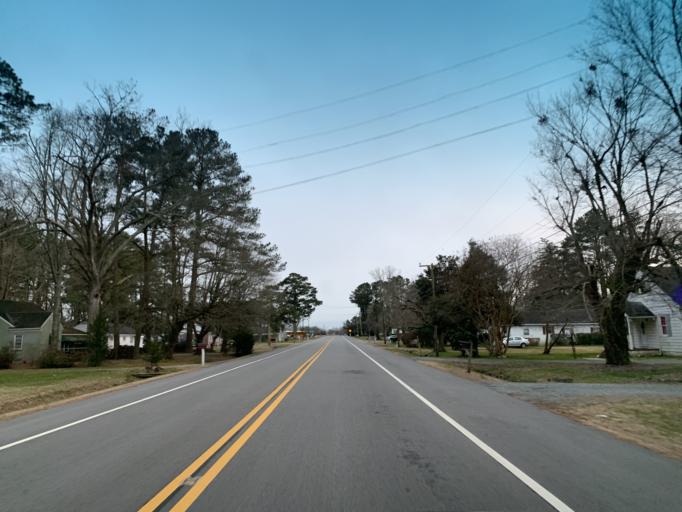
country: US
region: Maryland
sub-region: Worcester County
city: Pocomoke City
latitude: 38.0705
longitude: -75.5469
